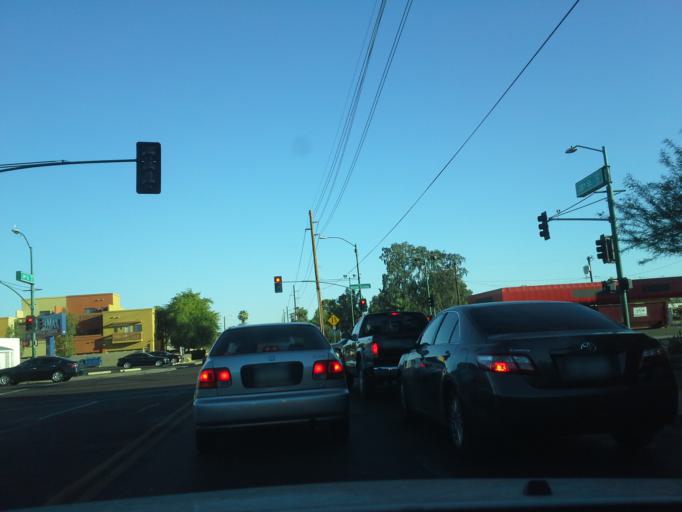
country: US
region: Arizona
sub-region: Maricopa County
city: Phoenix
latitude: 33.4954
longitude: -112.0216
